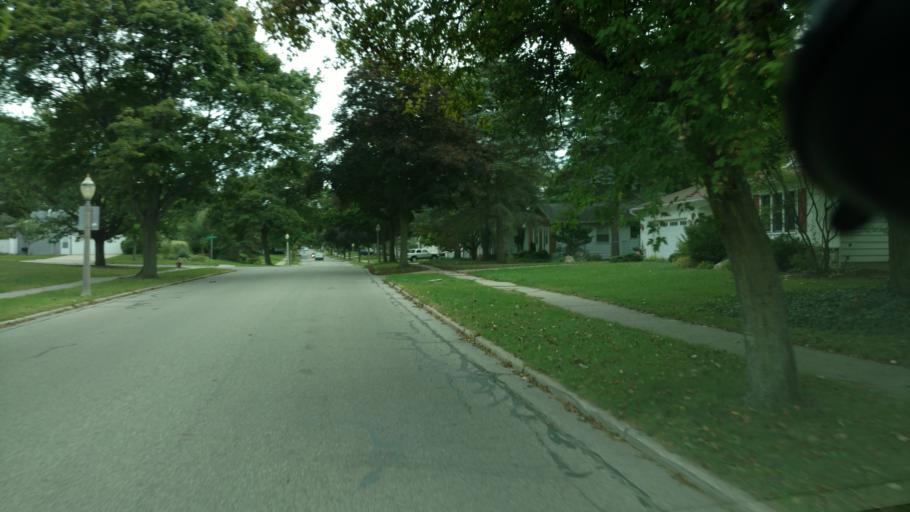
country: US
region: Michigan
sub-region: Ingham County
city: East Lansing
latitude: 42.7508
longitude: -84.5112
